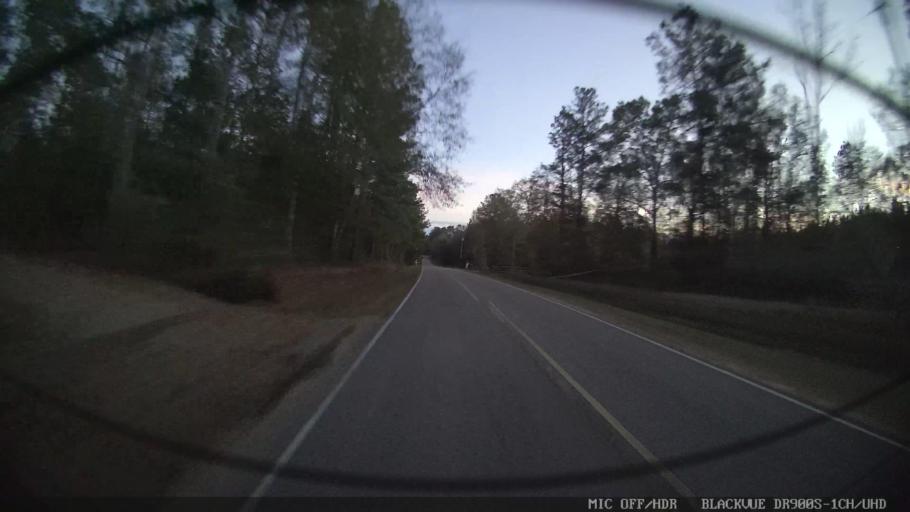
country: US
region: Mississippi
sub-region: Perry County
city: New Augusta
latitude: 31.1115
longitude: -89.1956
